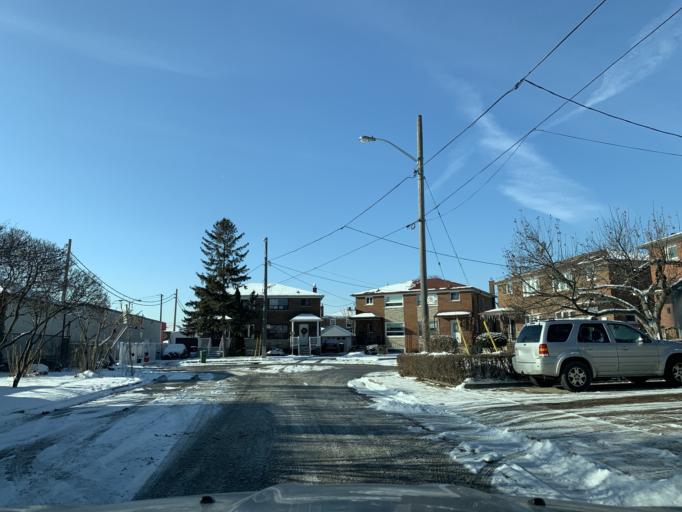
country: CA
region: Ontario
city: Toronto
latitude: 43.6703
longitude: -79.4826
